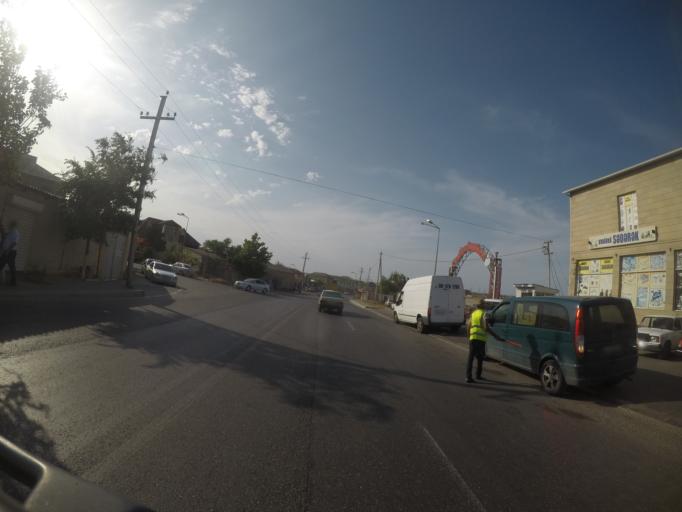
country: AZ
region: Baki
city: Binagadi
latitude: 40.4750
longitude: 49.8336
